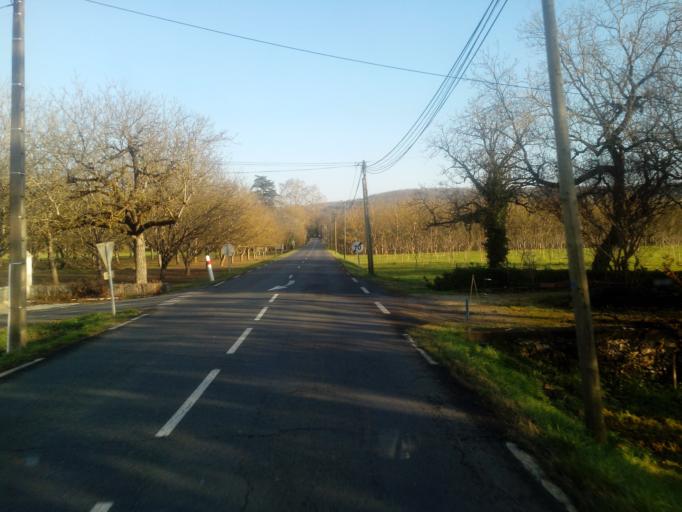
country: FR
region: Midi-Pyrenees
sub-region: Departement du Lot
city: Vayrac
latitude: 44.9081
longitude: 1.6319
